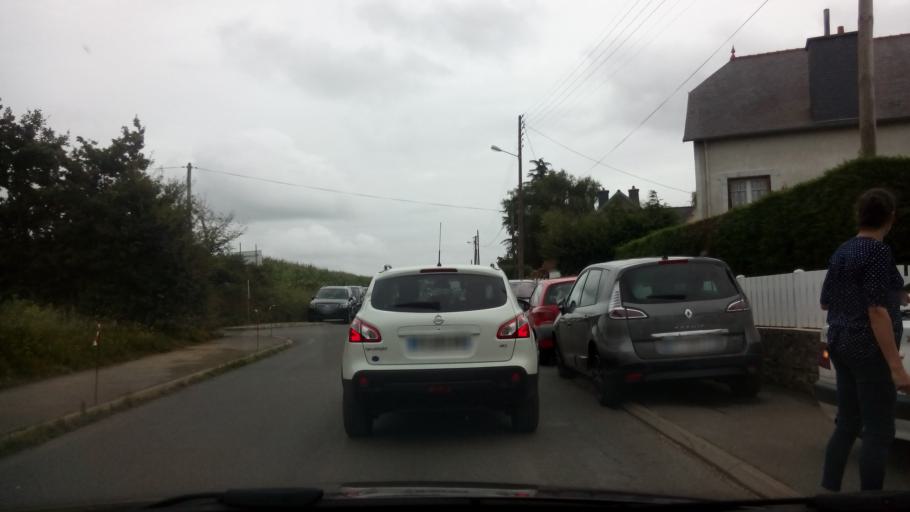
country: FR
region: Brittany
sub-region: Departement des Cotes-d'Armor
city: Plestin-les-Greves
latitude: 48.6681
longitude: -3.6360
